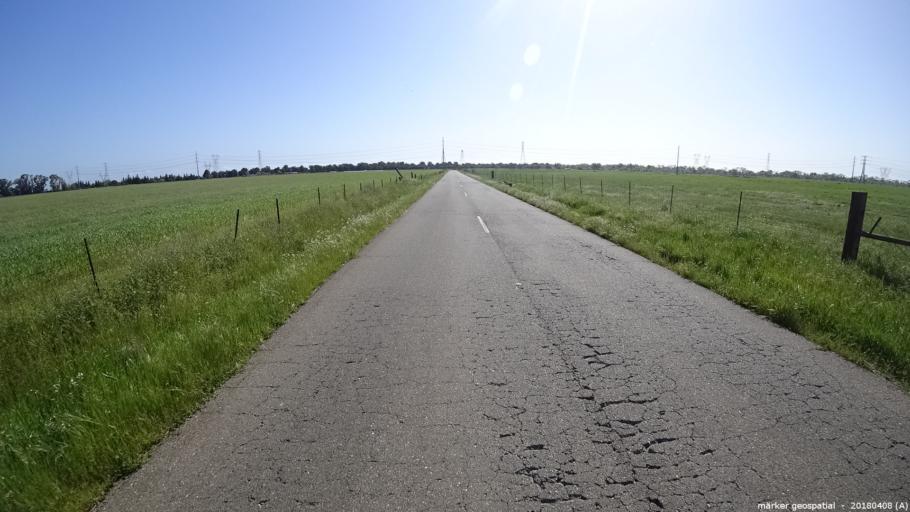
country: US
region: California
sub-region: Sacramento County
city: Elk Grove
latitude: 38.3618
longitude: -121.3583
